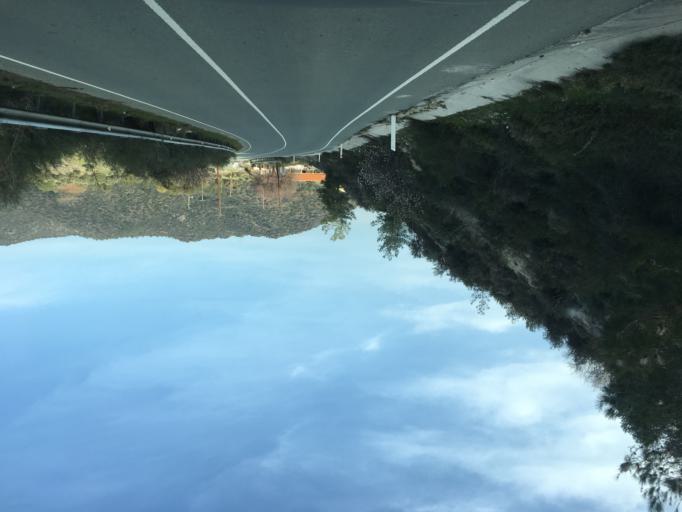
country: CY
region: Limassol
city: Pelendri
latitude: 34.8166
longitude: 32.9628
